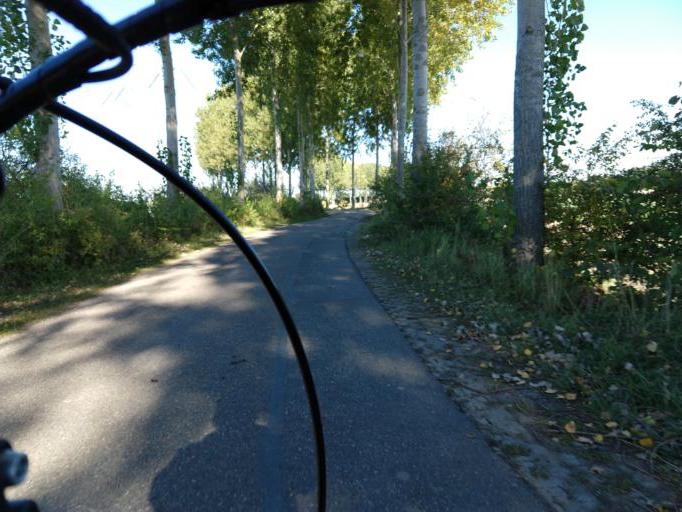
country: NL
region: Zeeland
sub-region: Gemeente Terneuzen
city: Terneuzen
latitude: 51.4147
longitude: 3.8334
